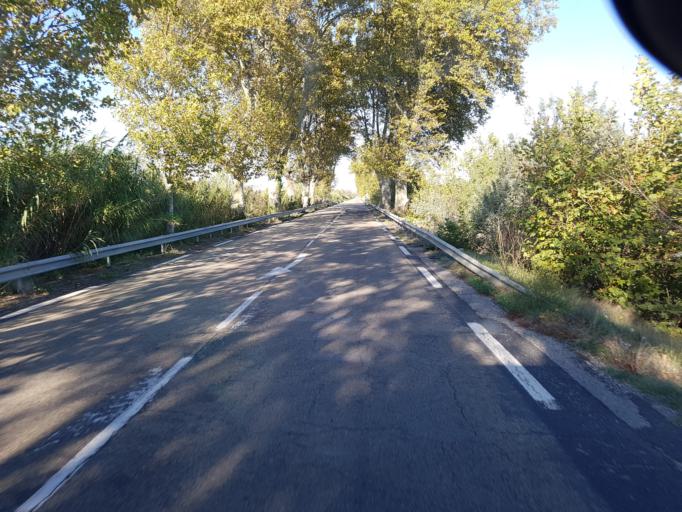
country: FR
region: Languedoc-Roussillon
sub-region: Departement de l'Aude
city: Coursan
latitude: 43.2435
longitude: 3.0631
